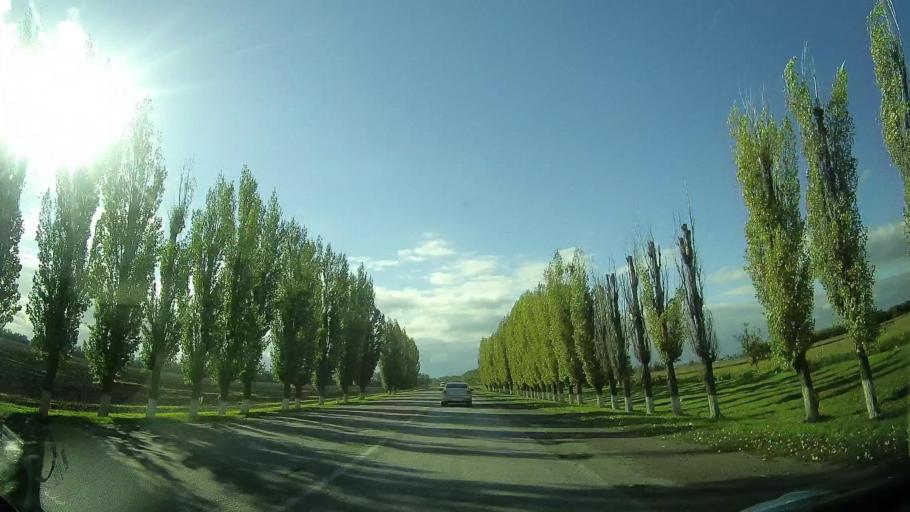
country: RU
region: Rostov
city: Tselina
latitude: 46.5325
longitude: 40.9980
